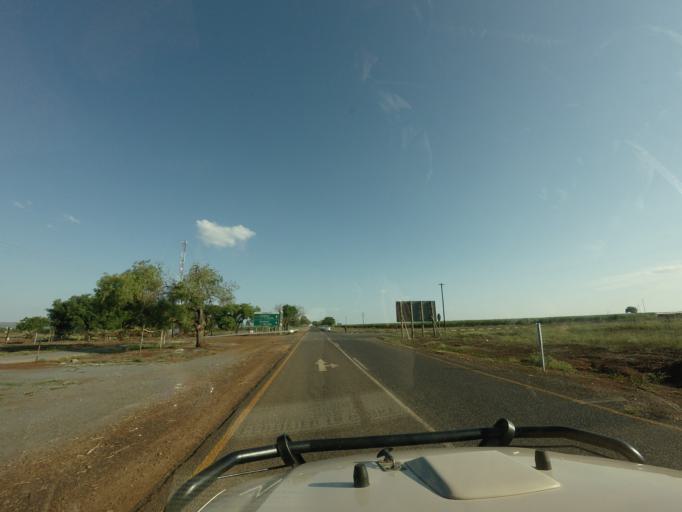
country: ZA
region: Mpumalanga
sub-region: Ehlanzeni District
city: Komatipoort
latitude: -25.3909
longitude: 31.9142
